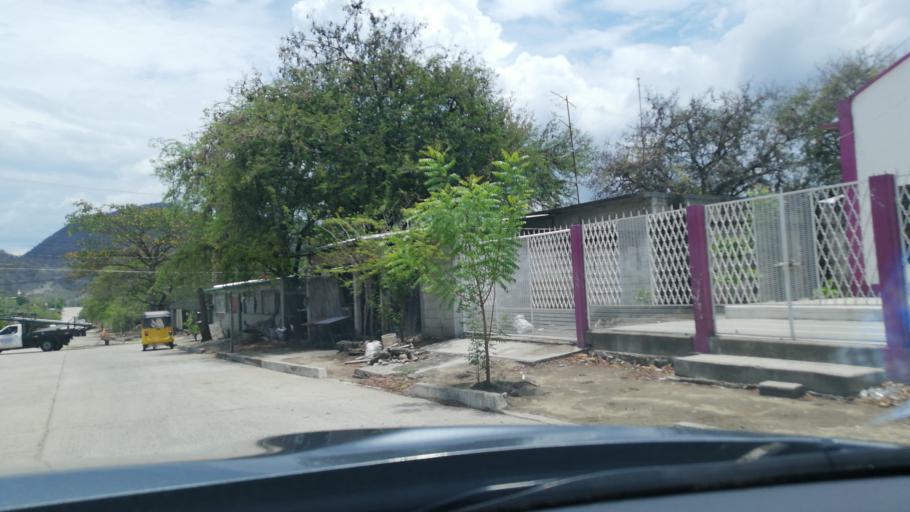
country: MX
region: Oaxaca
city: Santa Maria Jalapa del Marques
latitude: 16.4407
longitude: -95.4408
